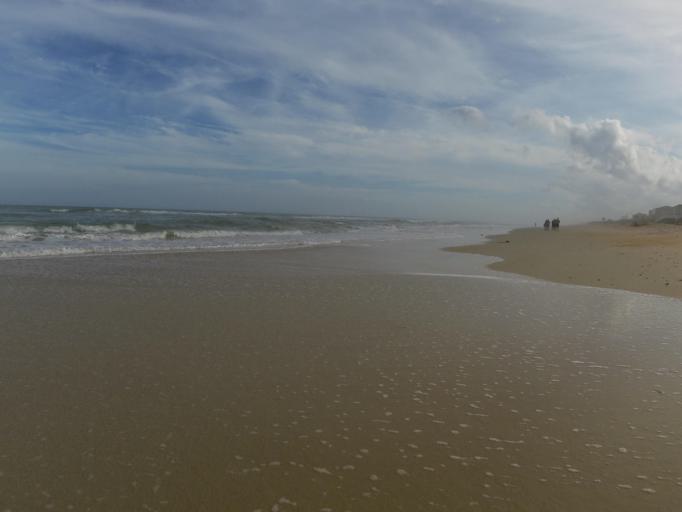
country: US
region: Florida
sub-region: Flagler County
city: Palm Coast
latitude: 29.6253
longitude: -81.1940
